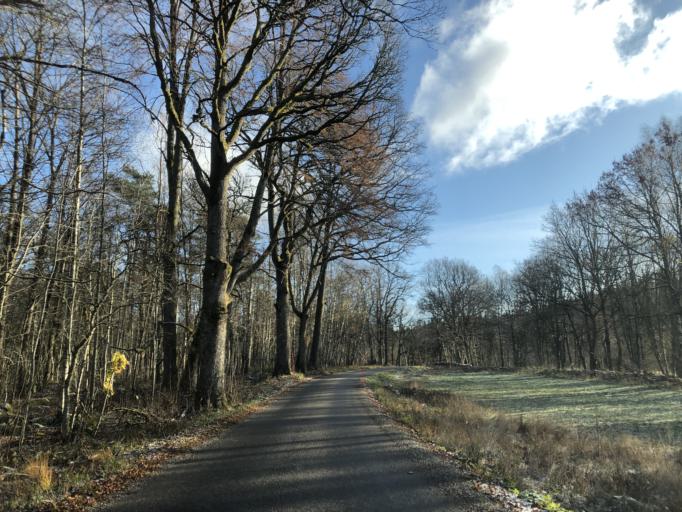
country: SE
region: Vaestra Goetaland
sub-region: Ulricehamns Kommun
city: Ulricehamn
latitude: 57.7273
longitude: 13.4211
